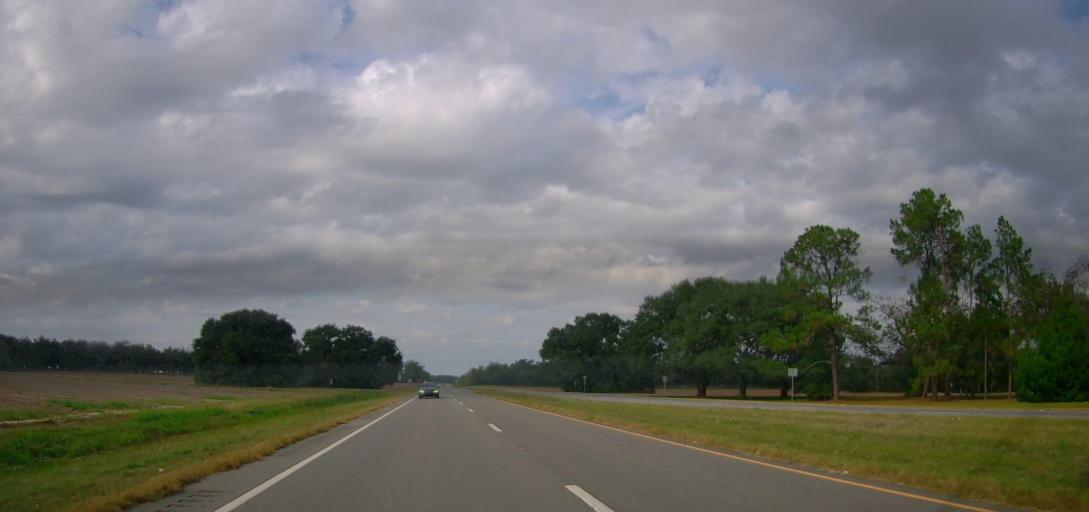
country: US
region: Georgia
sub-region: Thomas County
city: Meigs
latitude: 31.0308
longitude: -84.0627
